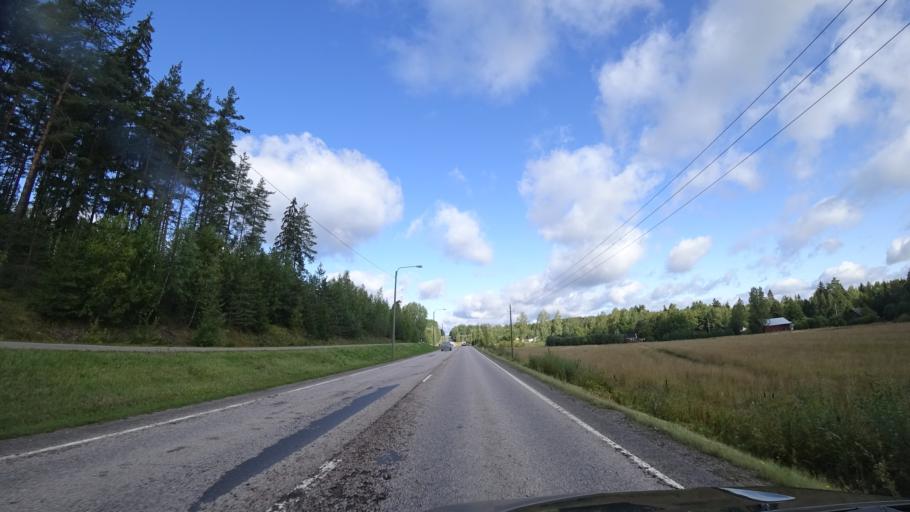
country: FI
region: Uusimaa
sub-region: Helsinki
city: Tuusula
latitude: 60.4324
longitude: 24.9897
